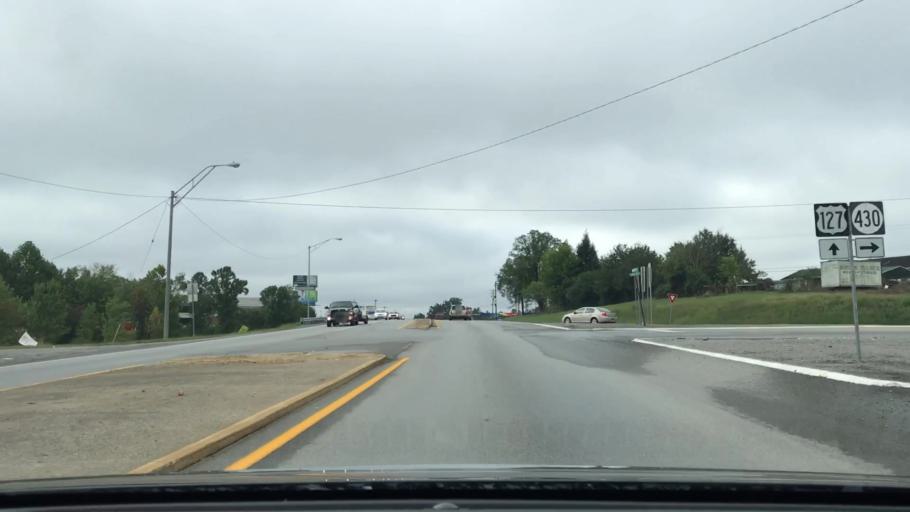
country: US
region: Kentucky
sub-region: Russell County
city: Russell Springs
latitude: 37.0388
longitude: -85.0745
